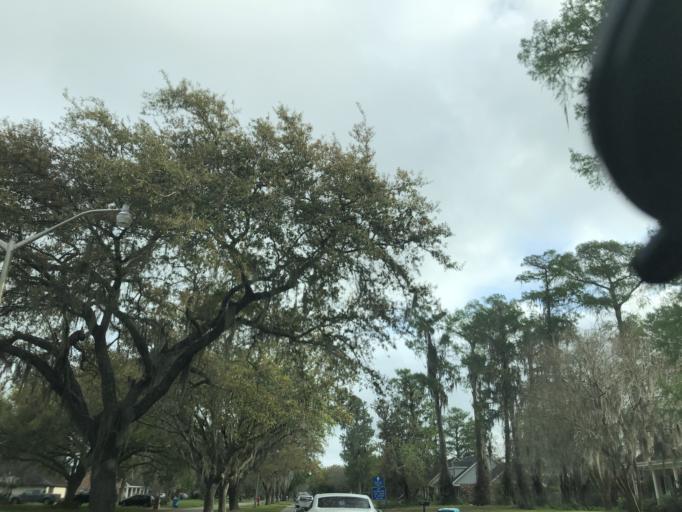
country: US
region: Louisiana
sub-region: Saint Charles Parish
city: New Sarpy
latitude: 29.9766
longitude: -90.3642
